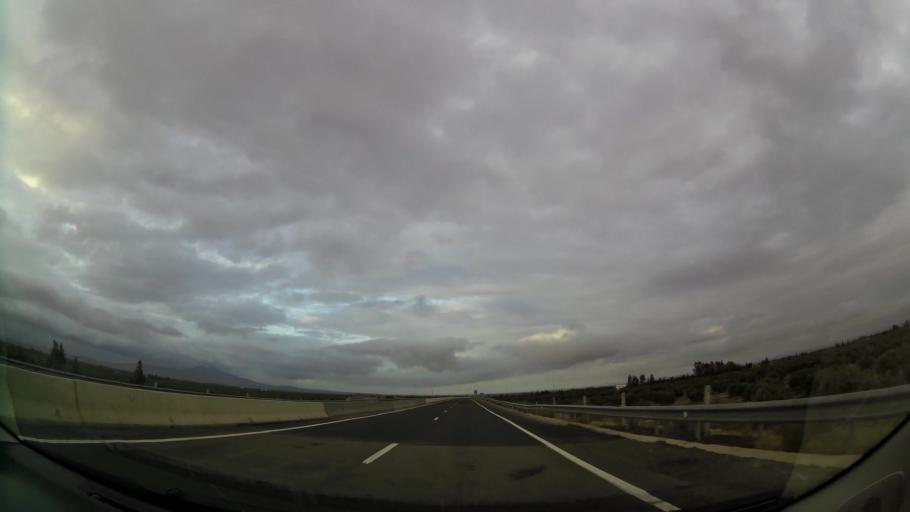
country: MA
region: Taza-Al Hoceima-Taounate
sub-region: Taza
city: Guercif
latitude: 34.3381
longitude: -3.3300
